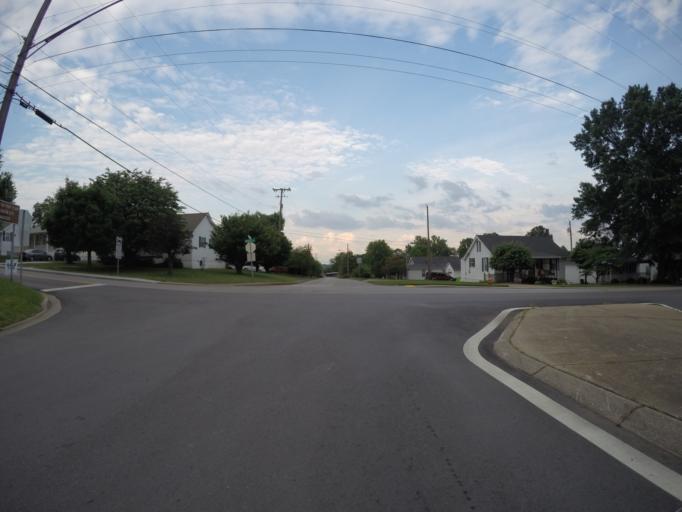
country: US
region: Tennessee
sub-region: Davidson County
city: Lakewood
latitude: 36.2641
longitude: -86.6478
